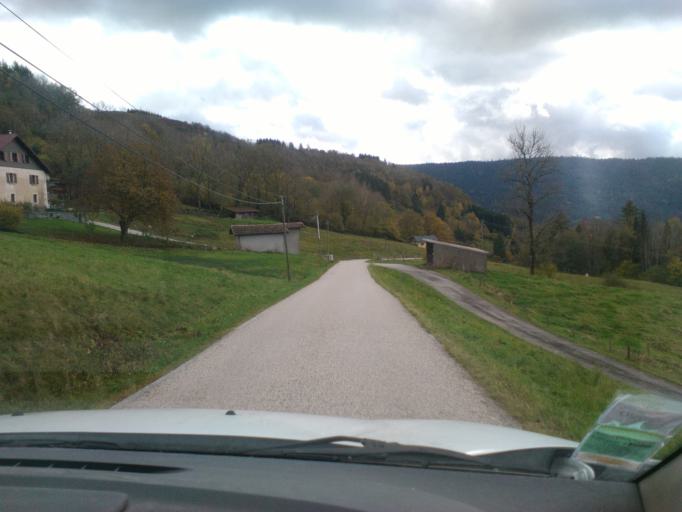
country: FR
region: Lorraine
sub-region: Departement des Vosges
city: Saulxures-sur-Moselotte
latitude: 47.9662
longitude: 6.7907
